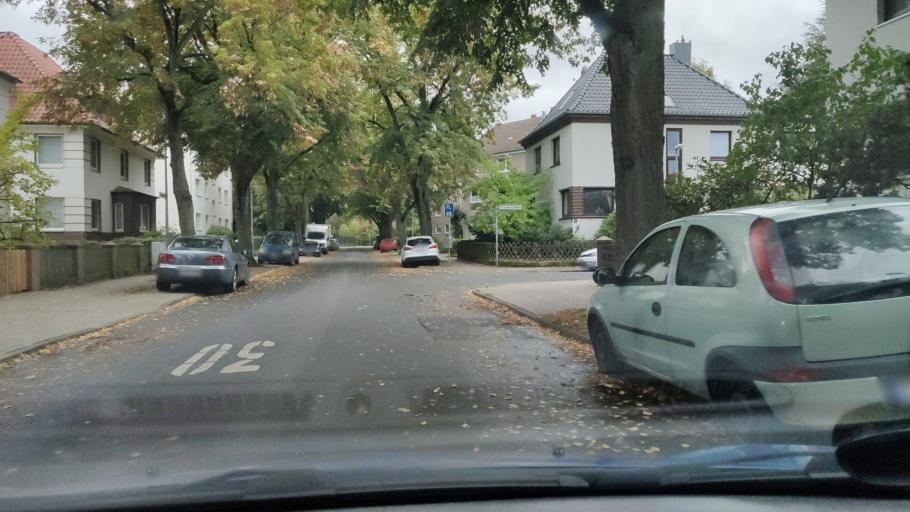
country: DE
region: Lower Saxony
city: Ronnenberg
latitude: 52.3811
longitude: 9.6691
